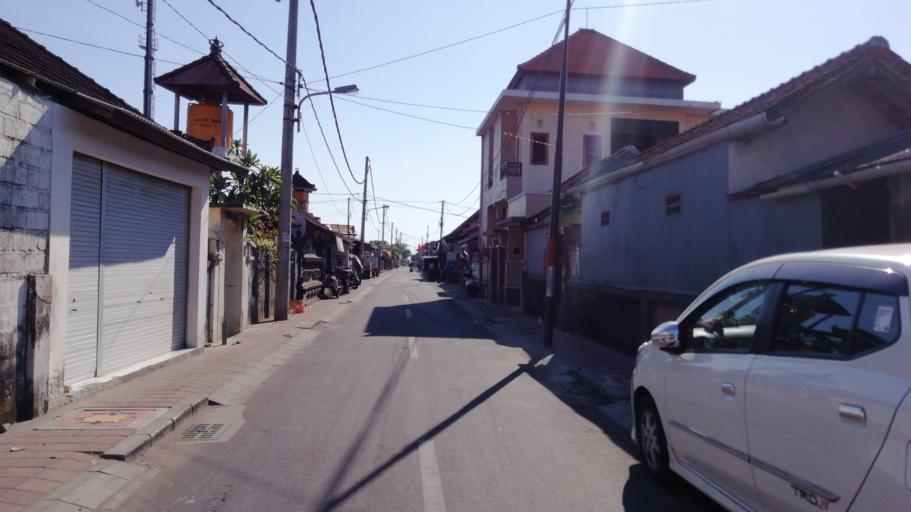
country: ID
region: Bali
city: Bualu
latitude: -8.7557
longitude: 115.2194
